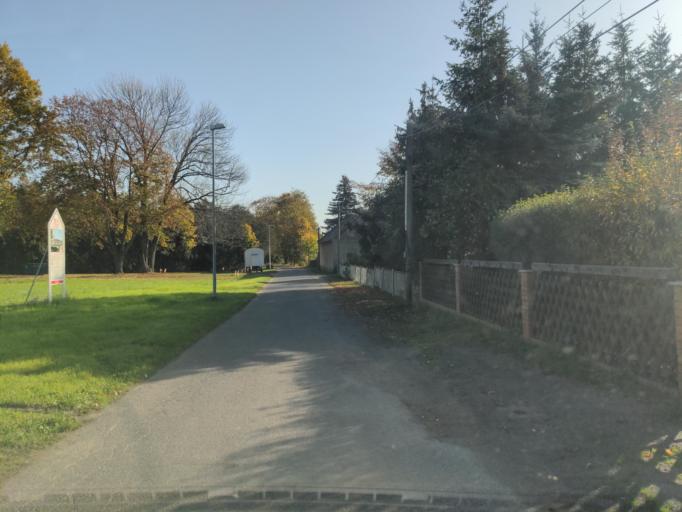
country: DE
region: Brandenburg
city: Cottbus
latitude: 51.6694
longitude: 14.3443
